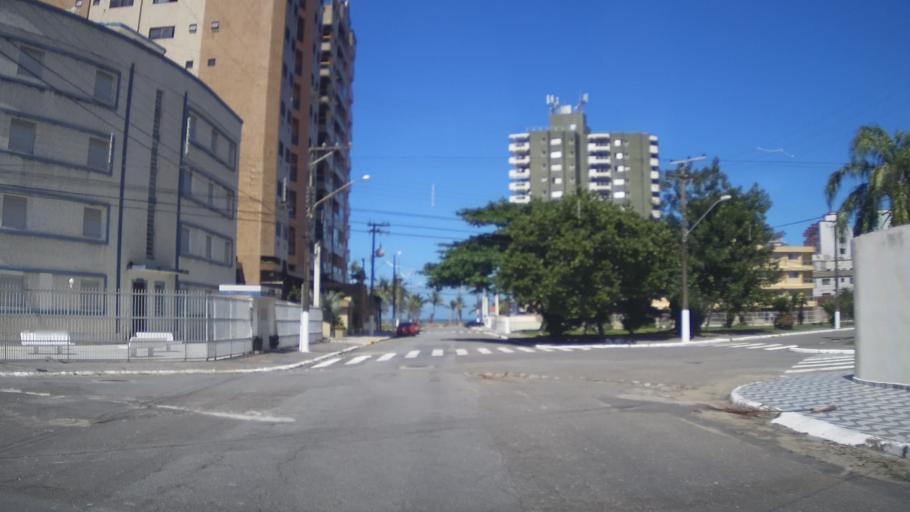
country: BR
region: Sao Paulo
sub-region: Mongagua
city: Mongagua
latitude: -24.0516
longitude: -46.5296
